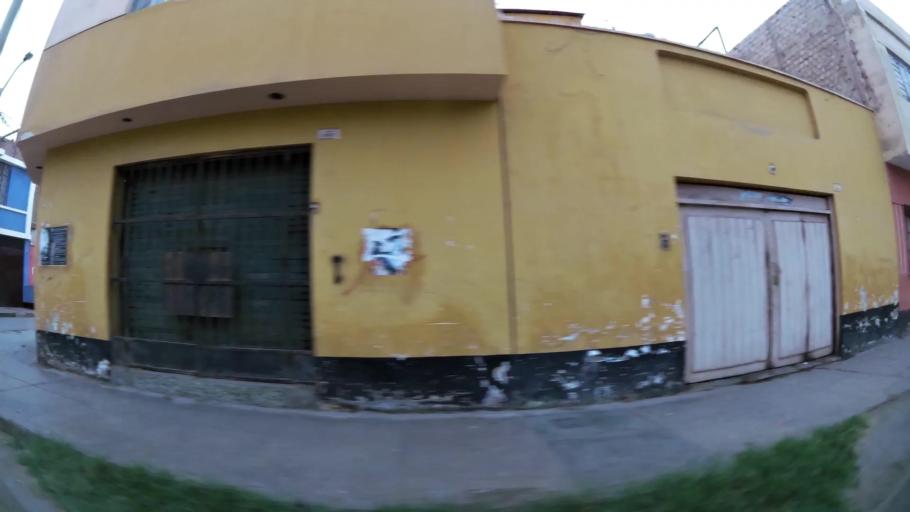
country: PE
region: Callao
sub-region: Callao
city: Callao
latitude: -12.0681
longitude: -77.1278
